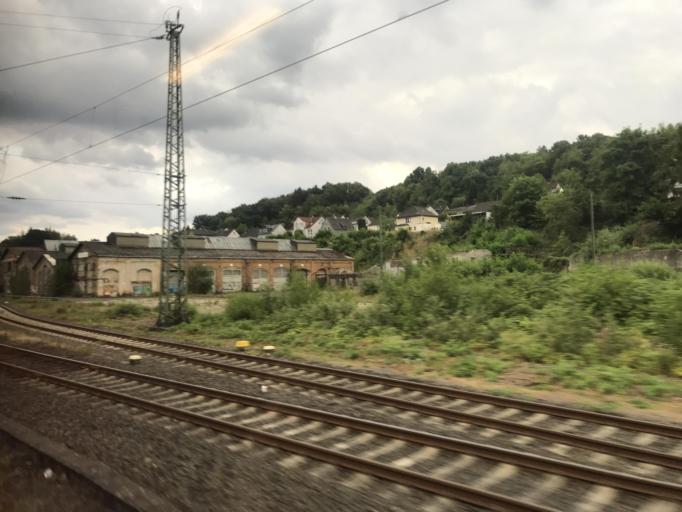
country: DE
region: Rheinland-Pfalz
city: Betzdorf
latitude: 50.7910
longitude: 7.8647
